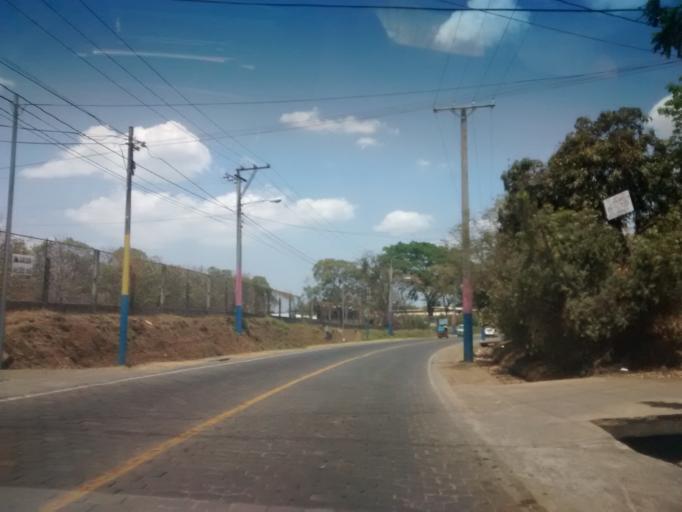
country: NI
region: Masaya
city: Ticuantepe
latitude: 12.0294
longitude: -86.2078
